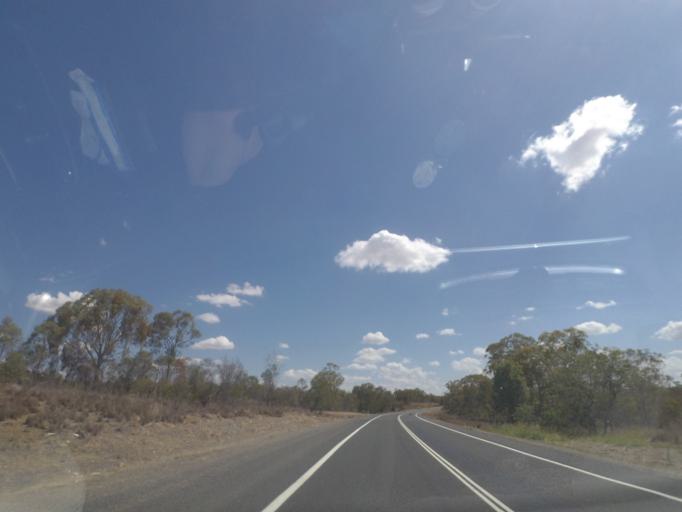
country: AU
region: Queensland
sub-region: Southern Downs
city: Warwick
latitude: -28.2270
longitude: 151.5518
